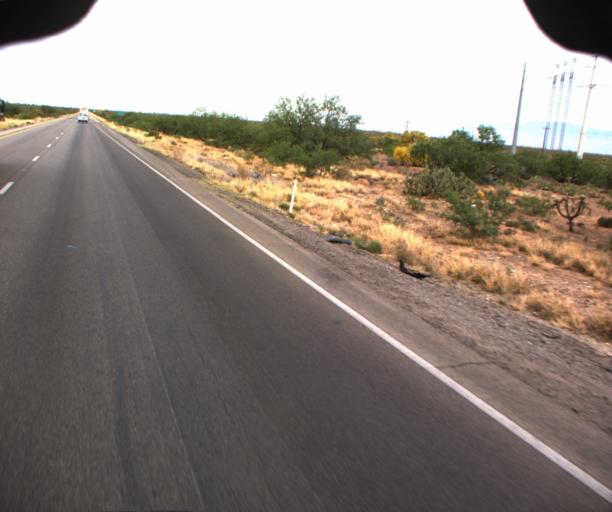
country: US
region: Arizona
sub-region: Pima County
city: Vail
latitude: 32.0319
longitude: -110.7253
